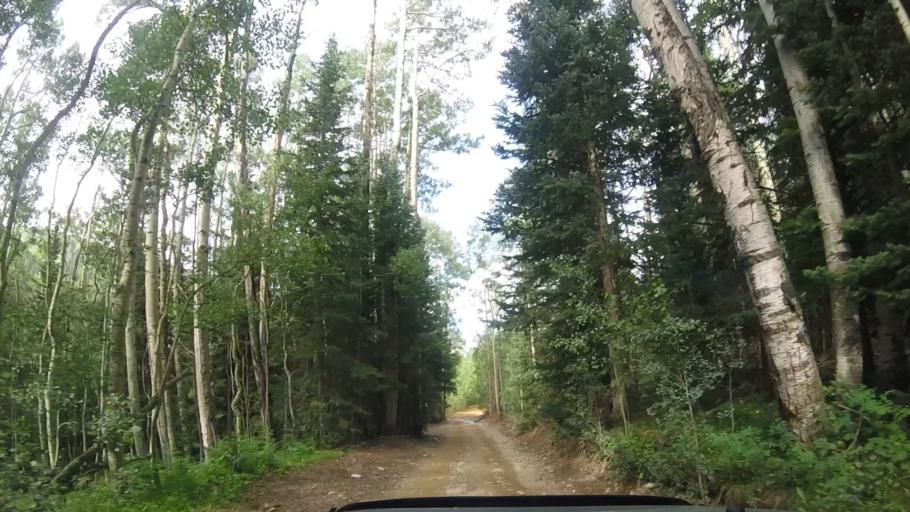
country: US
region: Colorado
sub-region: San Miguel County
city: Telluride
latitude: 37.8589
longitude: -107.8089
